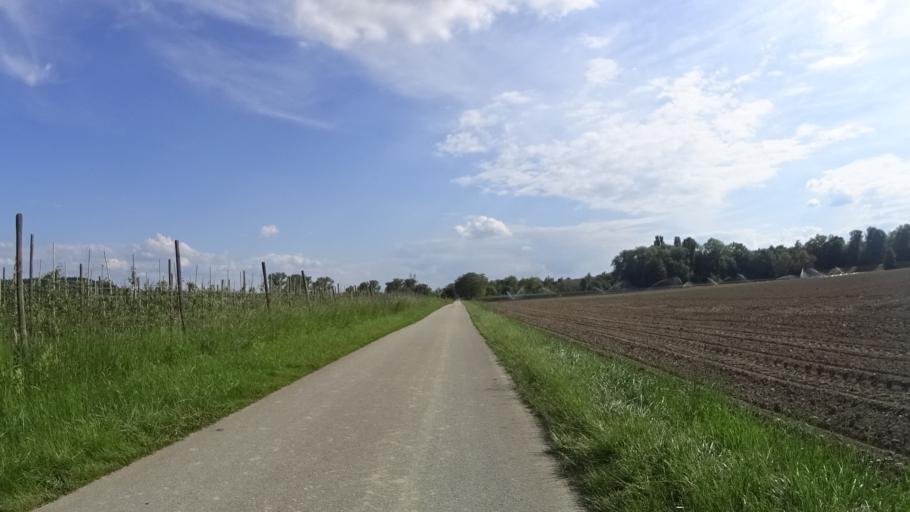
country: DE
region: Baden-Wuerttemberg
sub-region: Freiburg Region
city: Vogtsburg
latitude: 48.0859
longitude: 7.5935
